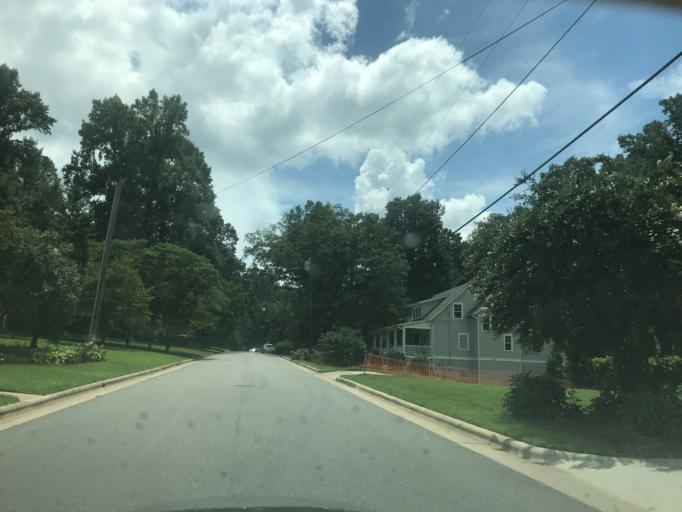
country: US
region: North Carolina
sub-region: Wake County
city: West Raleigh
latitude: 35.8202
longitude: -78.6376
